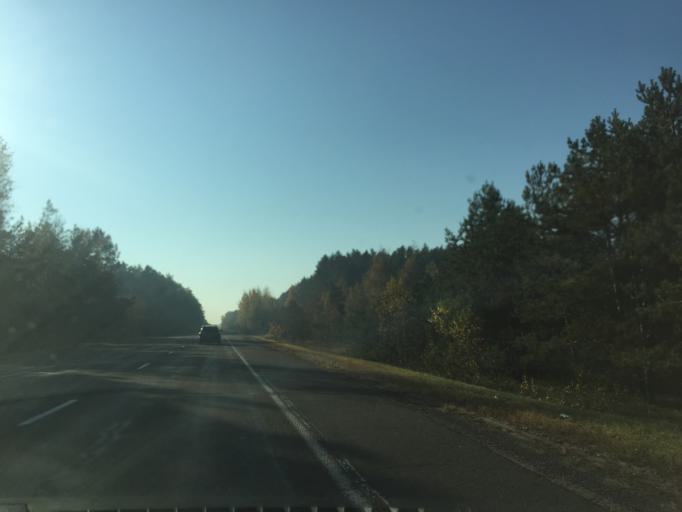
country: BY
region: Gomel
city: Kastsyukowka
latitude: 52.4353
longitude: 30.8265
